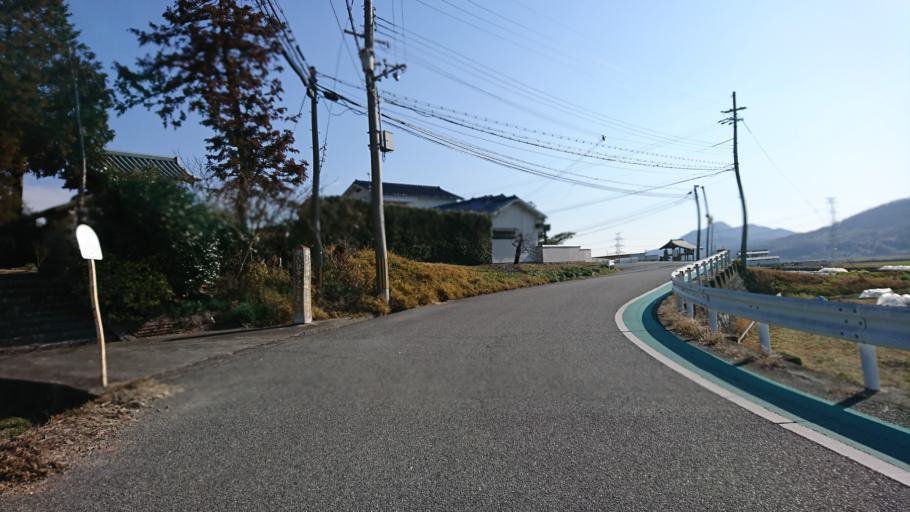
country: JP
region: Hyogo
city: Kakogawacho-honmachi
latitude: 34.8322
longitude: 134.8417
